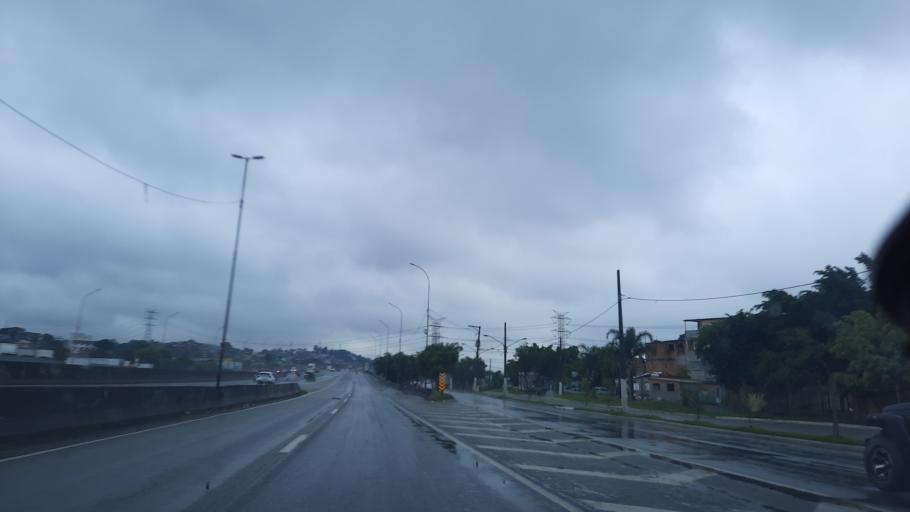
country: BR
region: Sao Paulo
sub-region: Guarulhos
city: Guarulhos
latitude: -23.4641
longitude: -46.5712
